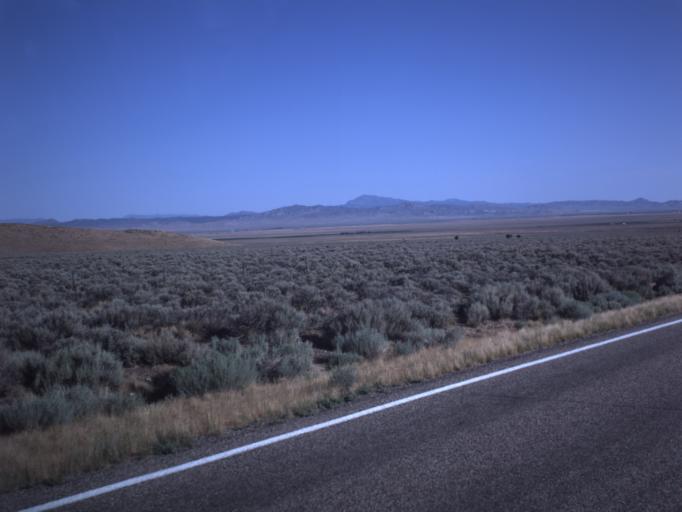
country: US
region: Utah
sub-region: Beaver County
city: Milford
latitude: 38.1450
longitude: -112.9598
